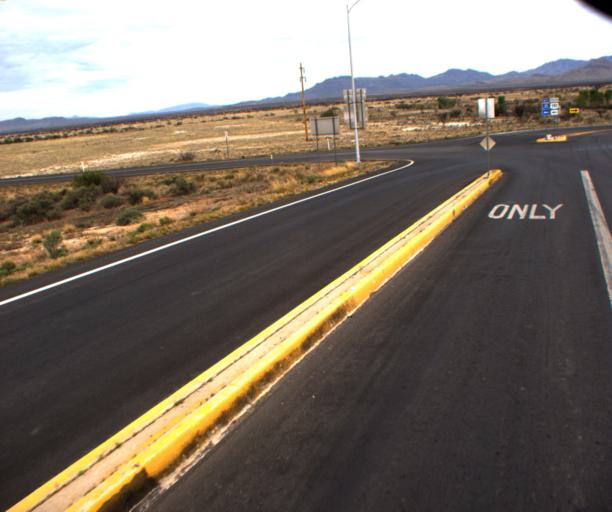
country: US
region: Arizona
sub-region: Cochise County
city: Willcox
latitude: 32.2231
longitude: -109.8793
